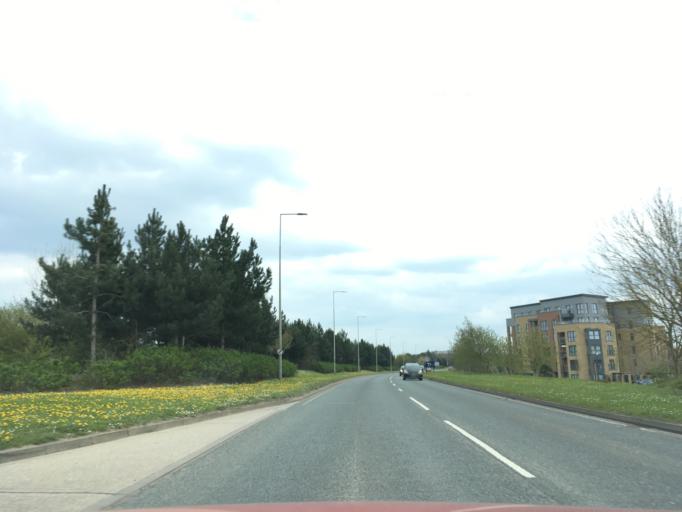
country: GB
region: England
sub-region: Milton Keynes
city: Broughton
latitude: 52.0424
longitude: -0.7157
